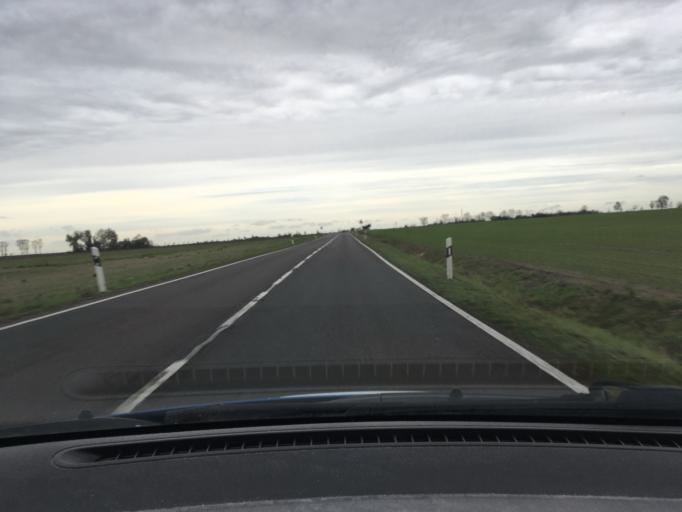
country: DE
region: Saxony-Anhalt
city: Leitzkau
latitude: 52.0402
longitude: 11.9771
